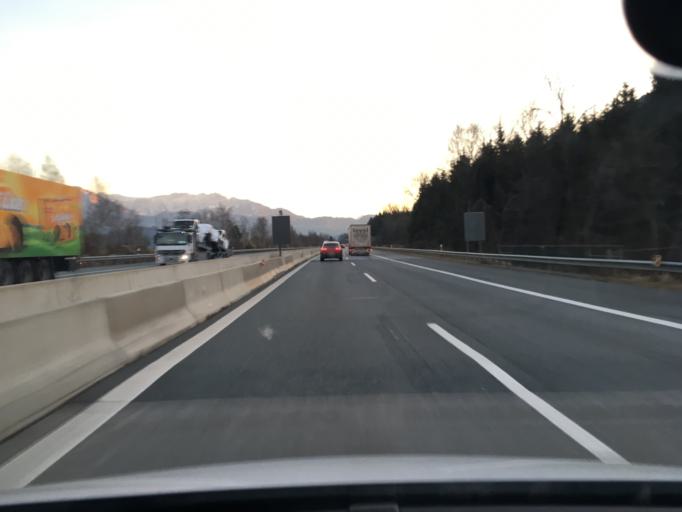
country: AT
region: Tyrol
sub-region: Politischer Bezirk Kufstein
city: Erl
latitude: 47.6970
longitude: 12.1619
